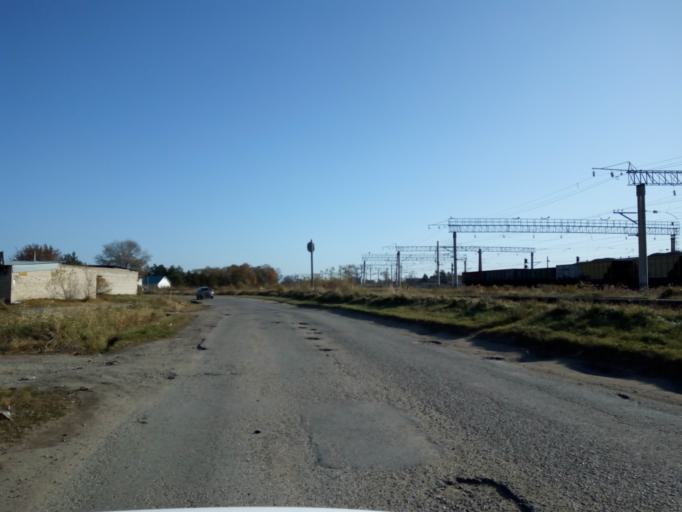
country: RU
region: Primorskiy
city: Dal'nerechensk
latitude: 45.9373
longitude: 133.7272
